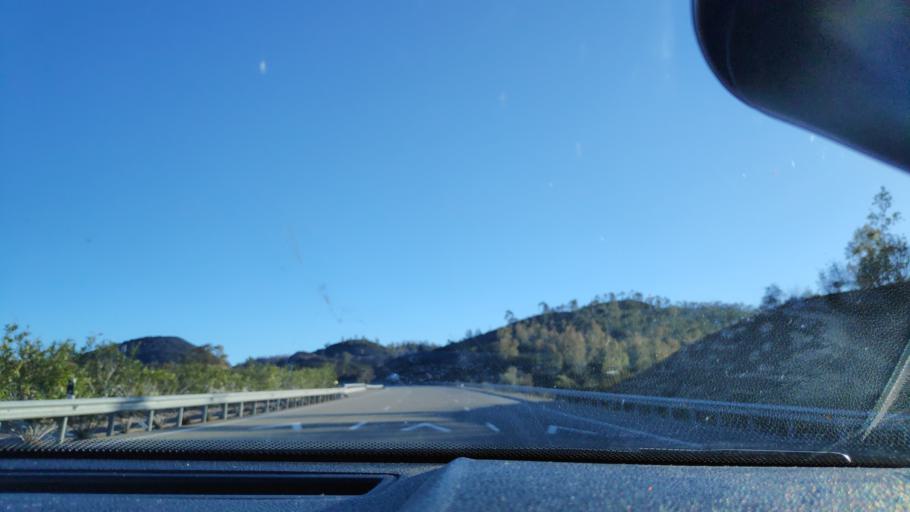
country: ES
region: Andalusia
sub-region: Provincia de Sevilla
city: El Ronquillo
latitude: 37.6681
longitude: -6.1706
